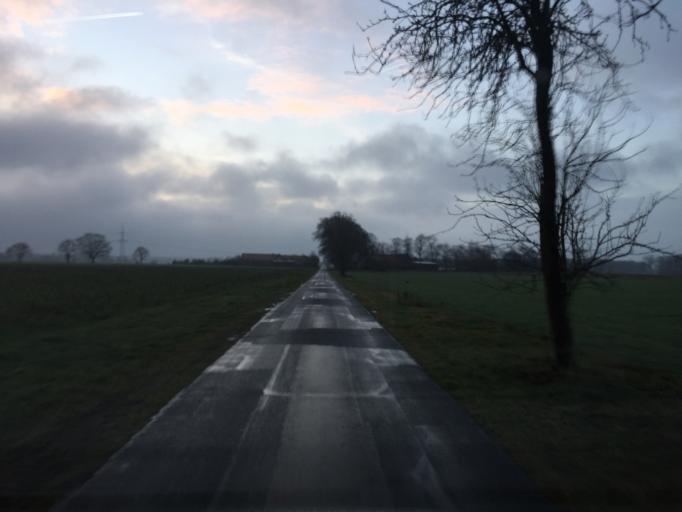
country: DE
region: Lower Saxony
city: Pennigsehl
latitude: 52.6616
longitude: 9.0198
